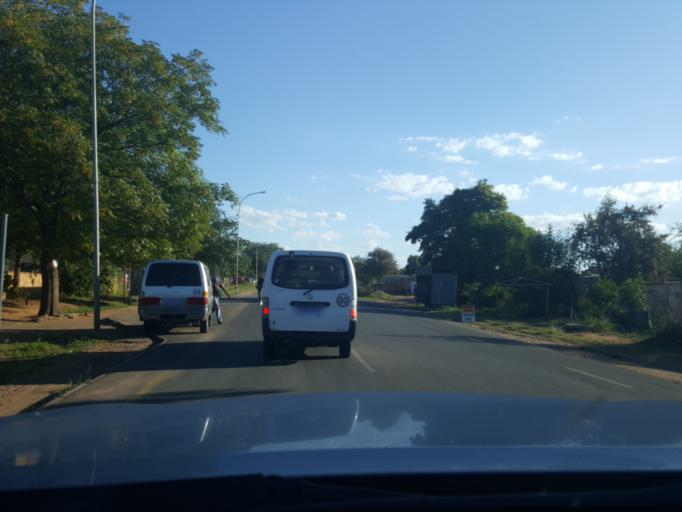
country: BW
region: South East
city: Gaborone
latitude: -24.6422
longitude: 25.9386
